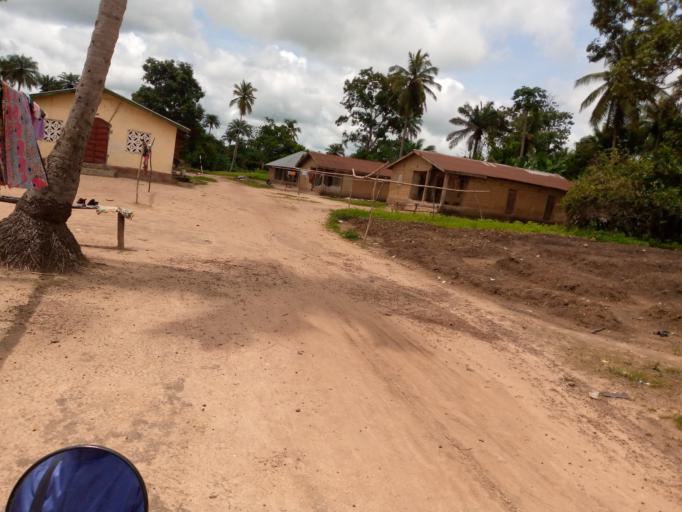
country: SL
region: Northern Province
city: Mange
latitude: 8.9908
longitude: -12.7955
